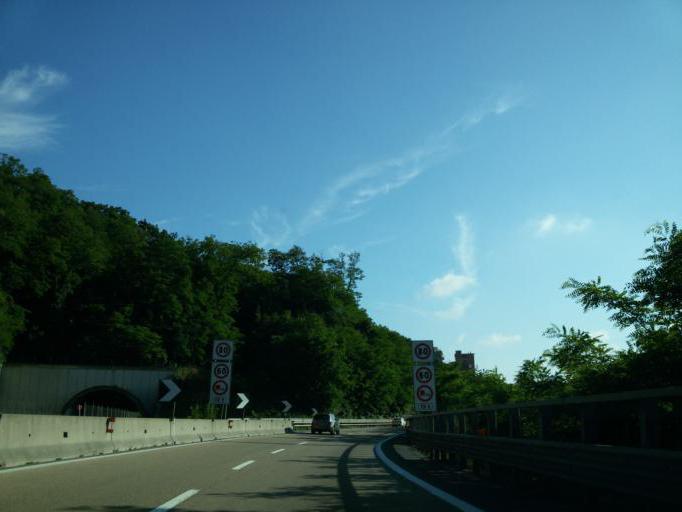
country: IT
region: Liguria
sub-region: Provincia di Genova
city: Manesseno
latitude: 44.4654
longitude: 8.9062
